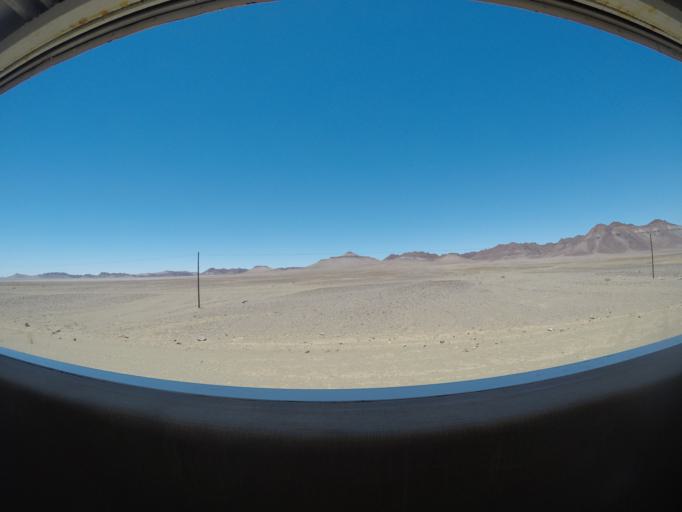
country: ZA
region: Northern Cape
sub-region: Namakwa District Municipality
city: Port Nolloth
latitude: -28.5994
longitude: 17.4844
